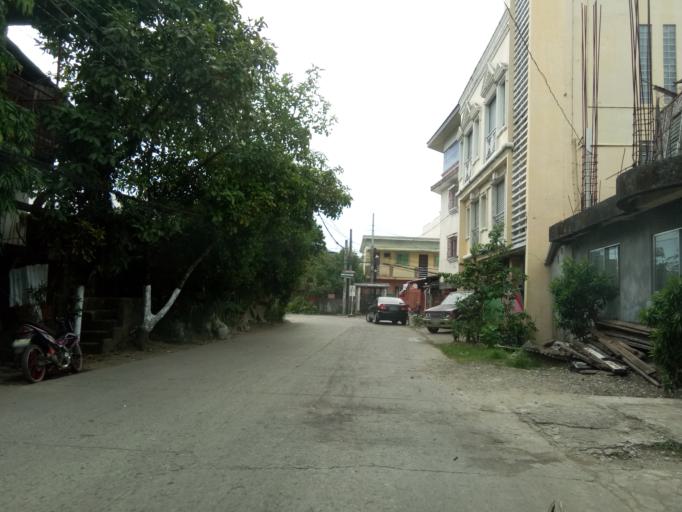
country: PH
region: Caraga
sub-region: Province of Surigao del Norte
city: Surigao
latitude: 9.7841
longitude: 125.4868
